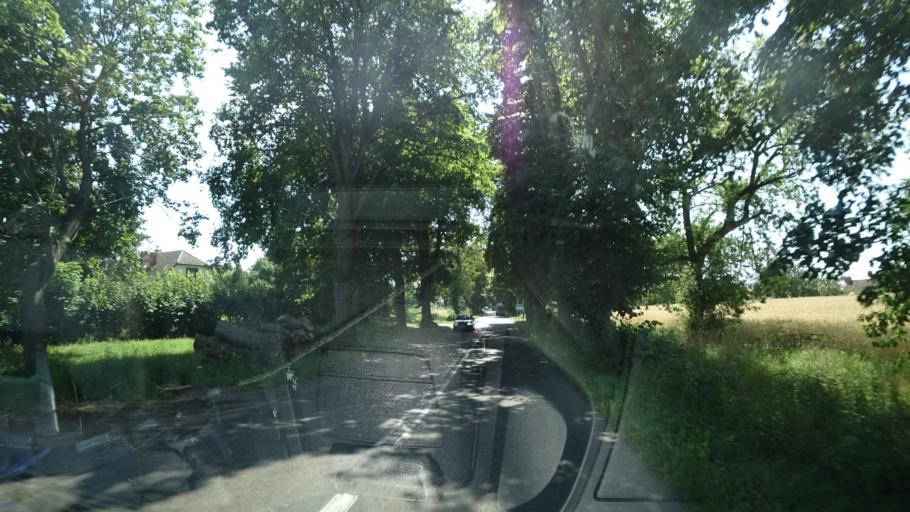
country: PL
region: West Pomeranian Voivodeship
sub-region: Powiat lobeski
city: Lobez
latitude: 53.6504
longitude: 15.6140
